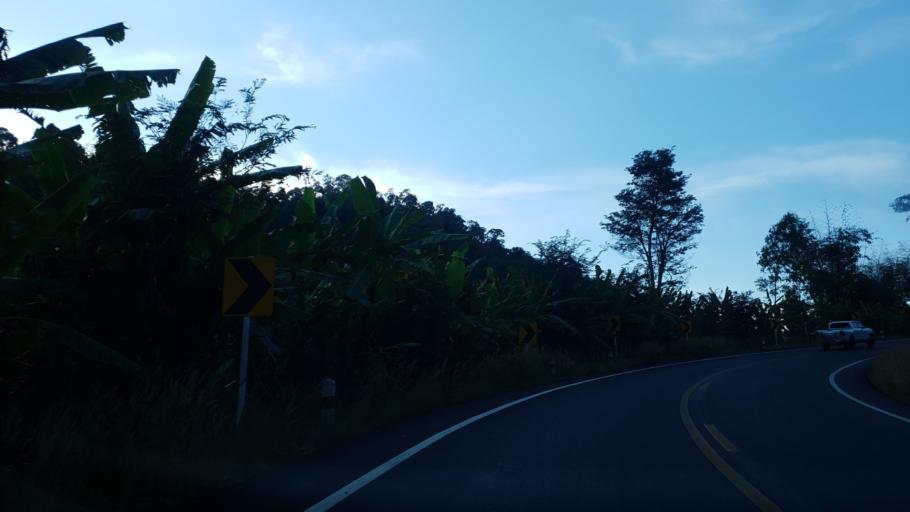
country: TH
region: Loei
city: Dan Sai
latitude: 17.2272
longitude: 101.0587
